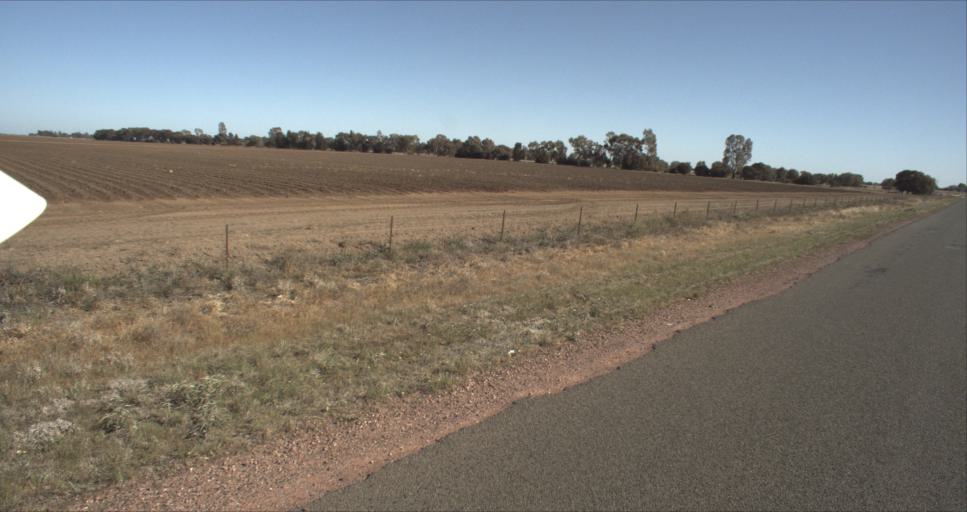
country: AU
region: New South Wales
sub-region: Leeton
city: Leeton
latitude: -34.5689
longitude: 146.2639
